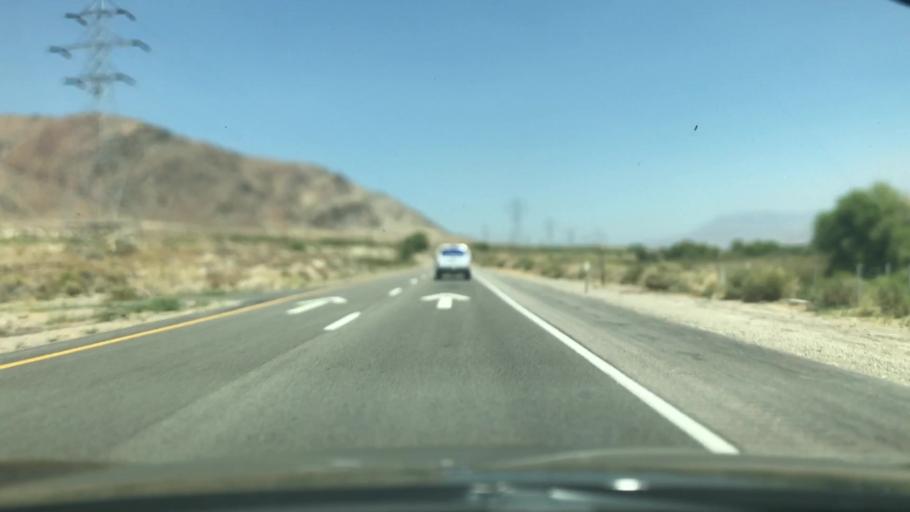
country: US
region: California
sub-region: Inyo County
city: Lone Pine
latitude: 36.6598
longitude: -118.0912
